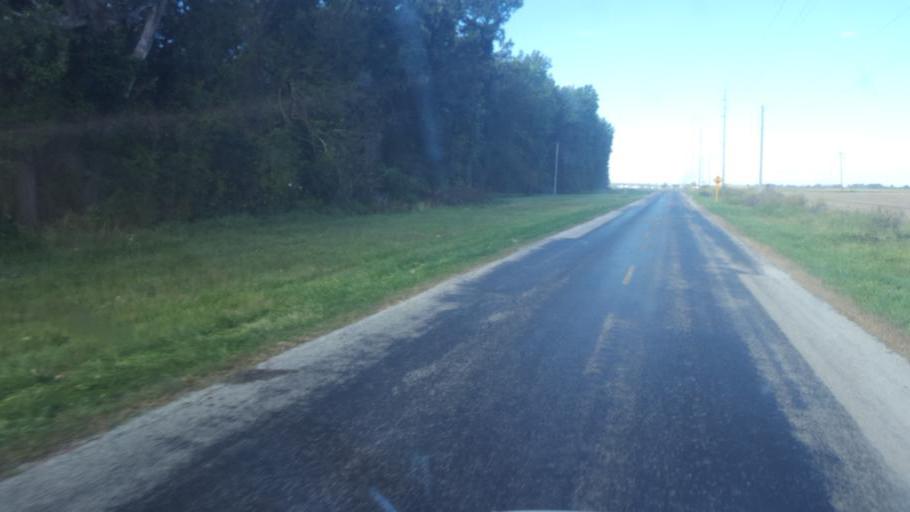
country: US
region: Ohio
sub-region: Marion County
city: Marion
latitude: 40.6884
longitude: -83.0881
